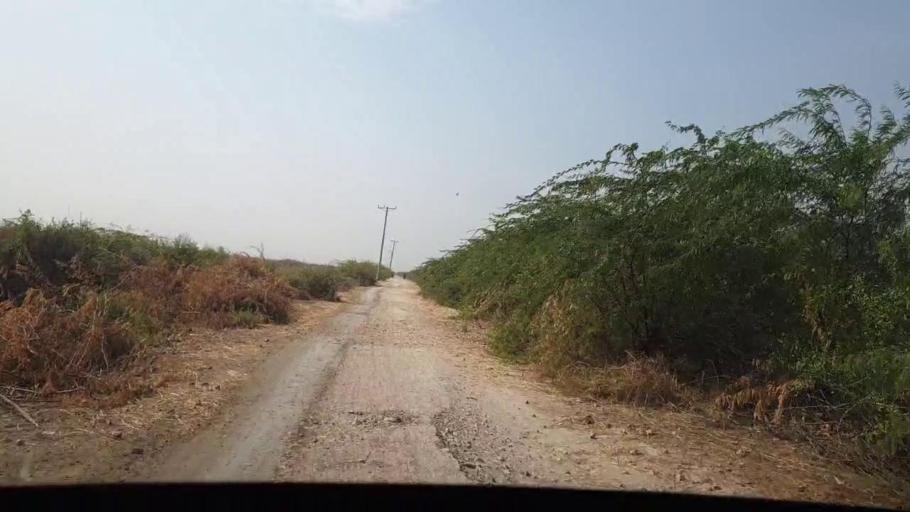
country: PK
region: Sindh
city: Chuhar Jamali
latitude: 24.2713
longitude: 67.8972
